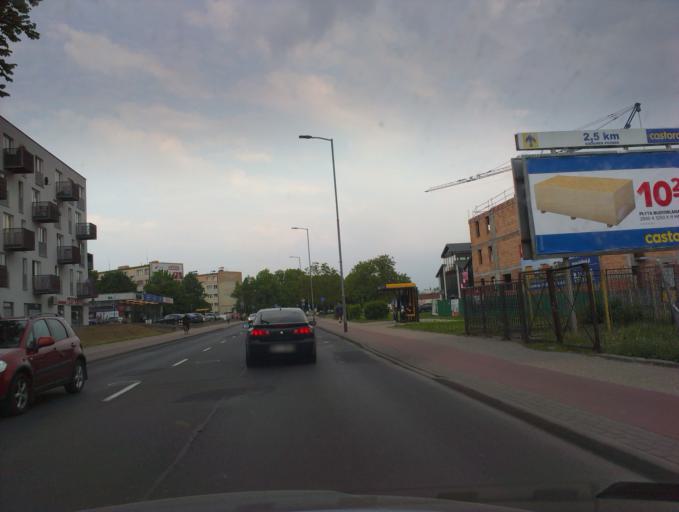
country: PL
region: West Pomeranian Voivodeship
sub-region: Koszalin
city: Koszalin
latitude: 54.1930
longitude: 16.2098
